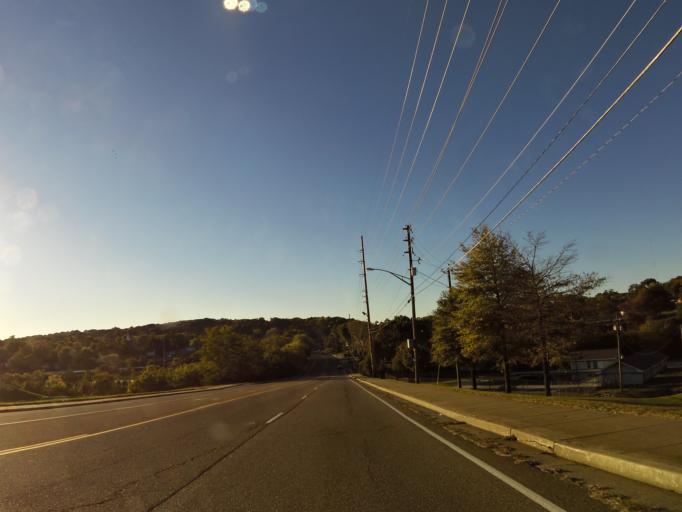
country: US
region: Tennessee
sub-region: Knox County
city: Knoxville
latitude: 35.9681
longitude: -83.9489
